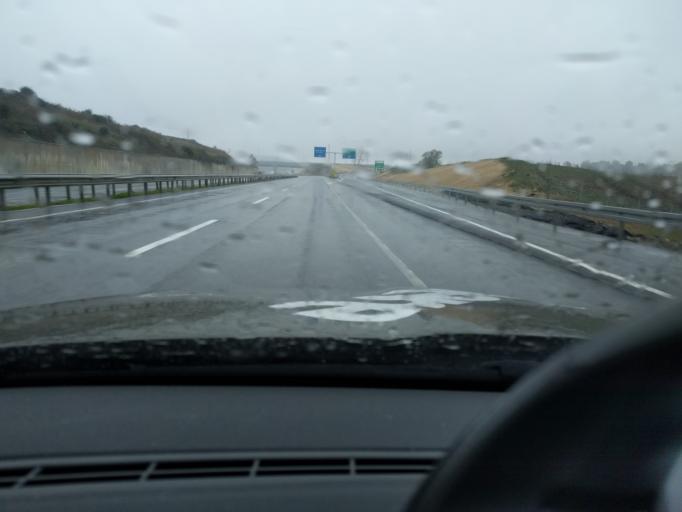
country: TR
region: Istanbul
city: Durusu
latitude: 41.2611
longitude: 28.6773
